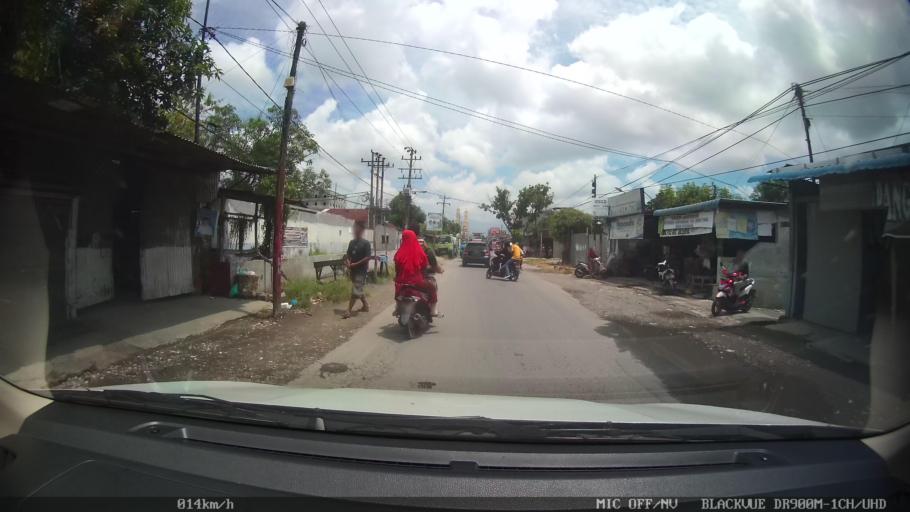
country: ID
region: North Sumatra
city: Medan
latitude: 3.6178
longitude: 98.7482
